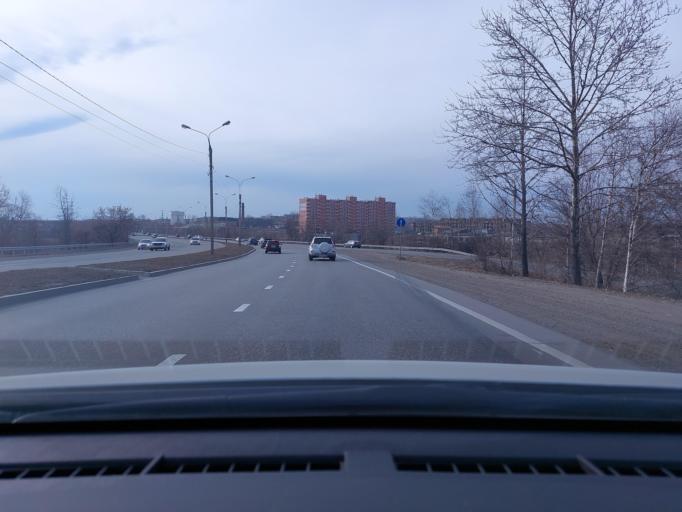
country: RU
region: Irkutsk
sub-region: Irkutskiy Rayon
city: Irkutsk
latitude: 52.3250
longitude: 104.2120
